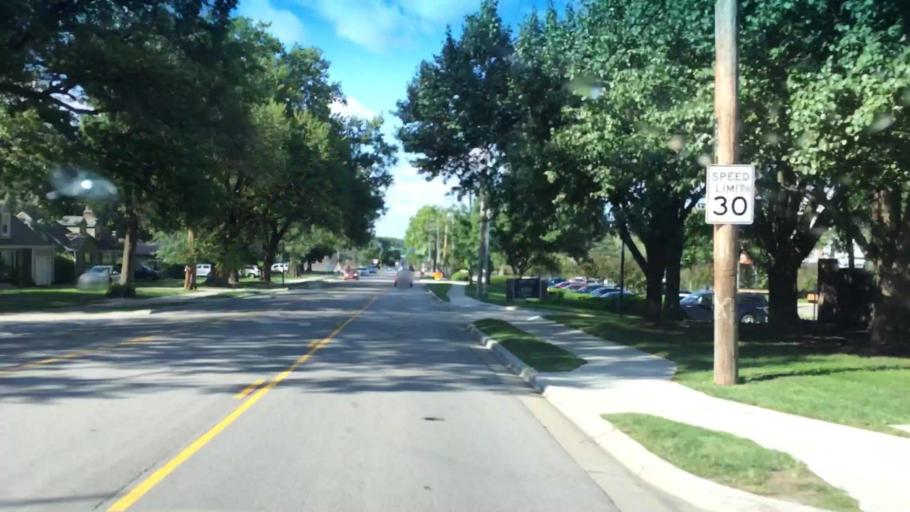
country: US
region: Kansas
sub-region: Johnson County
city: Prairie Village
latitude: 38.9987
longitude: -94.6304
